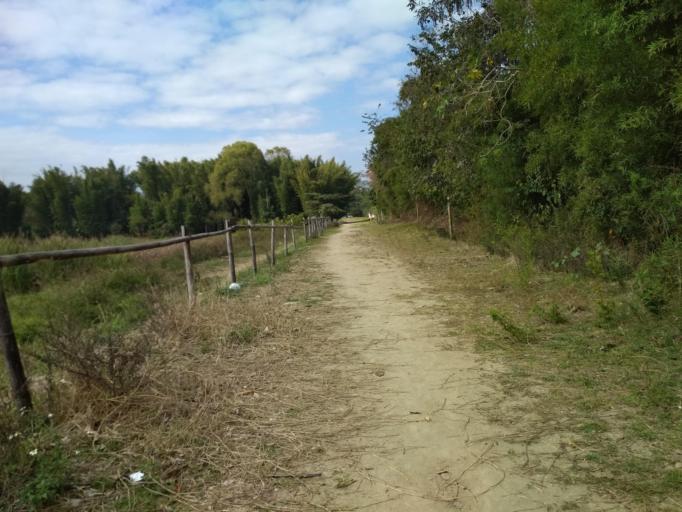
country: MX
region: Veracruz
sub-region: Coatepec
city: Tuzamapan
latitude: 19.3705
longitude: -96.8791
